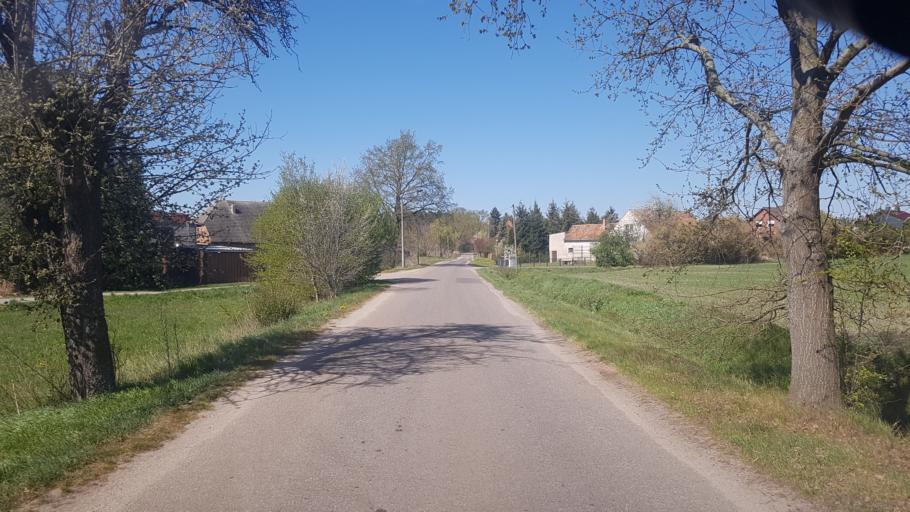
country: DE
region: Brandenburg
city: Sonnewalde
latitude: 51.7134
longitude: 13.6286
